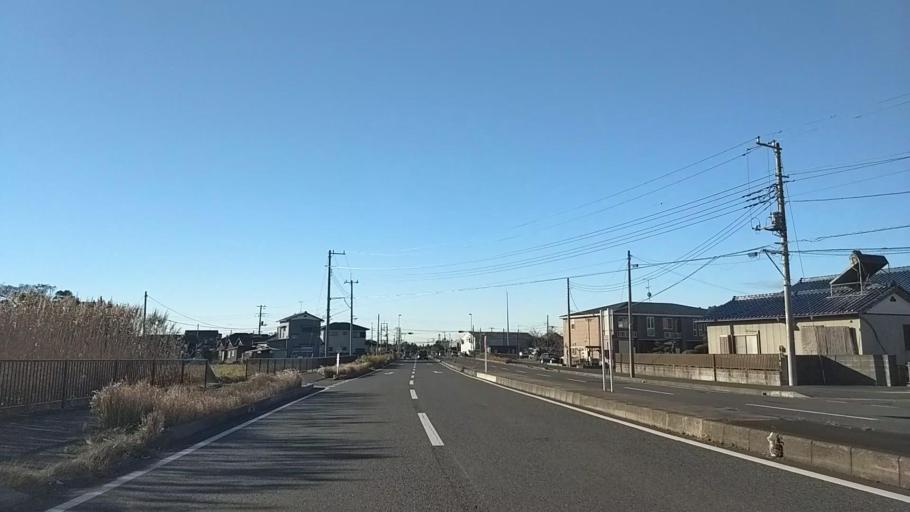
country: JP
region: Chiba
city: Kisarazu
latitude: 35.3968
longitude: 139.9208
